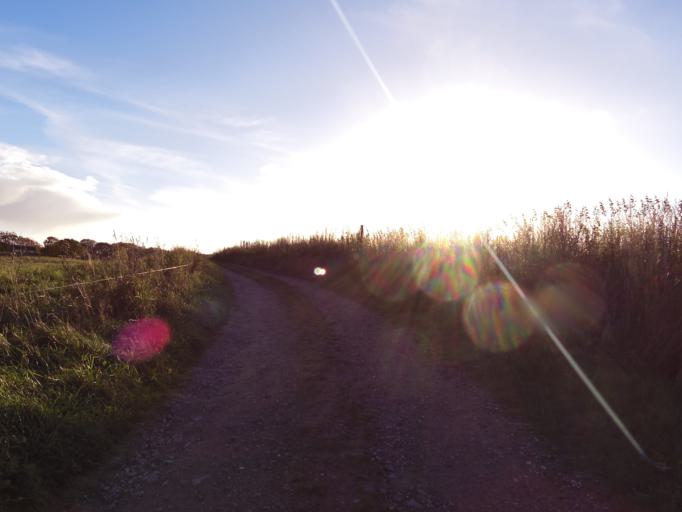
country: DK
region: Central Jutland
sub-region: Arhus Kommune
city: Framlev
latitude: 56.1296
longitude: 10.0289
